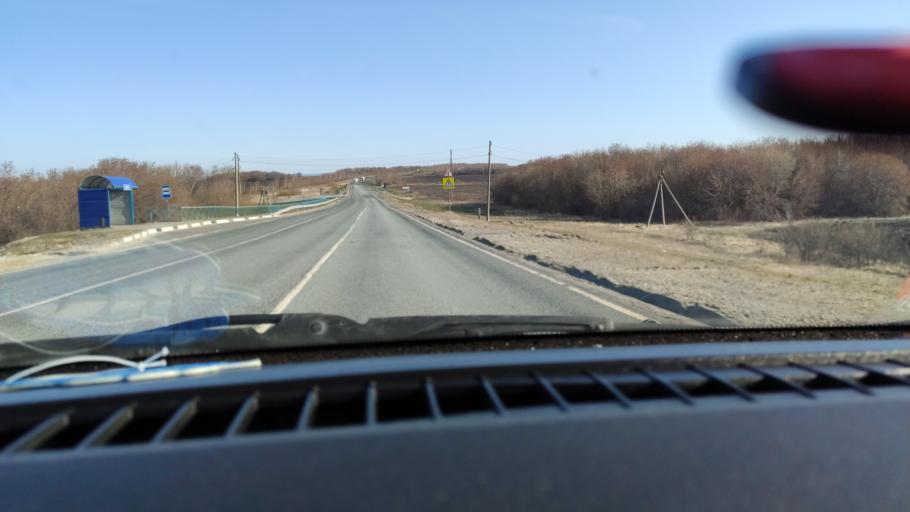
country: RU
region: Samara
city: Syzran'
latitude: 52.9684
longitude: 48.3080
